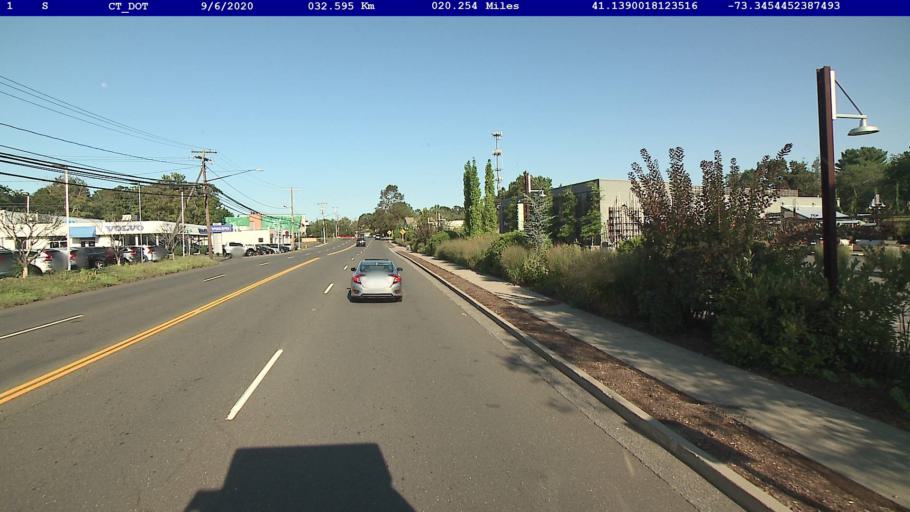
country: US
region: Connecticut
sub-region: Fairfield County
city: Westport
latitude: 41.1390
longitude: -73.3455
